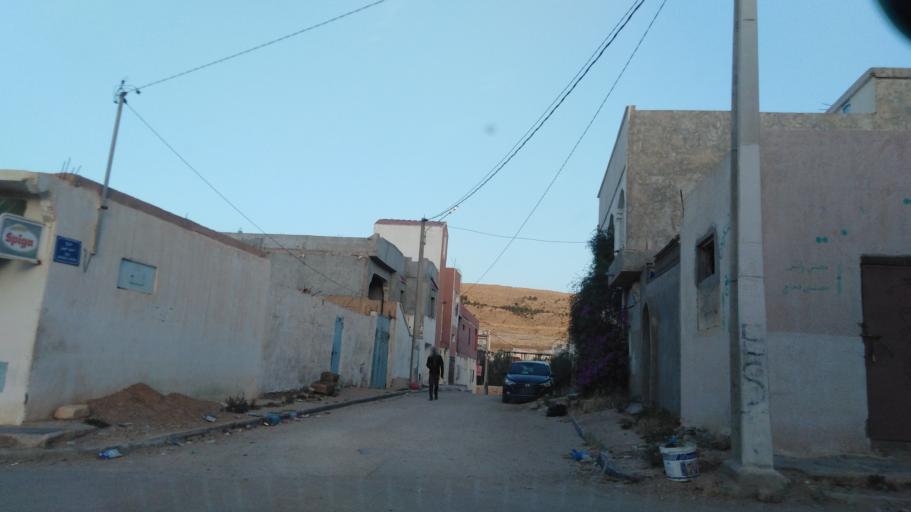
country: TN
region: Tataouine
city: Tataouine
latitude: 32.9403
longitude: 10.4577
